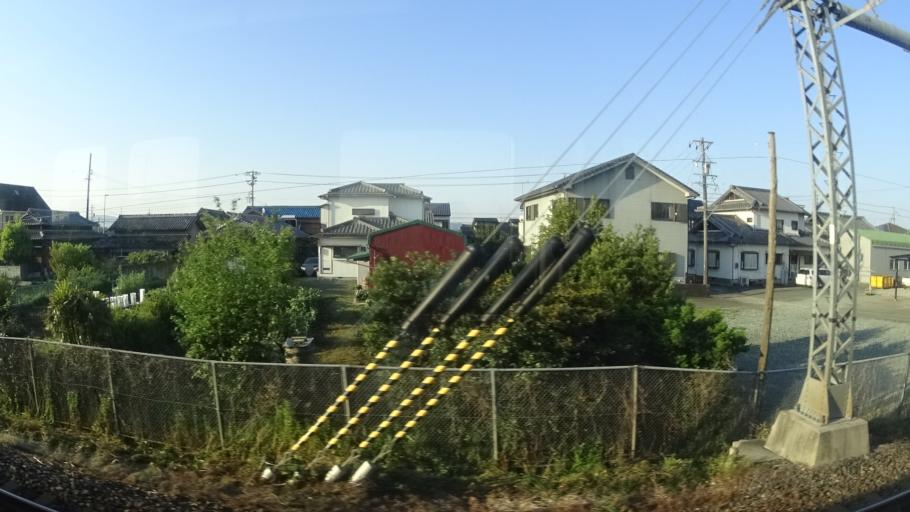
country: JP
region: Mie
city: Ise
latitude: 34.5373
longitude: 136.6222
